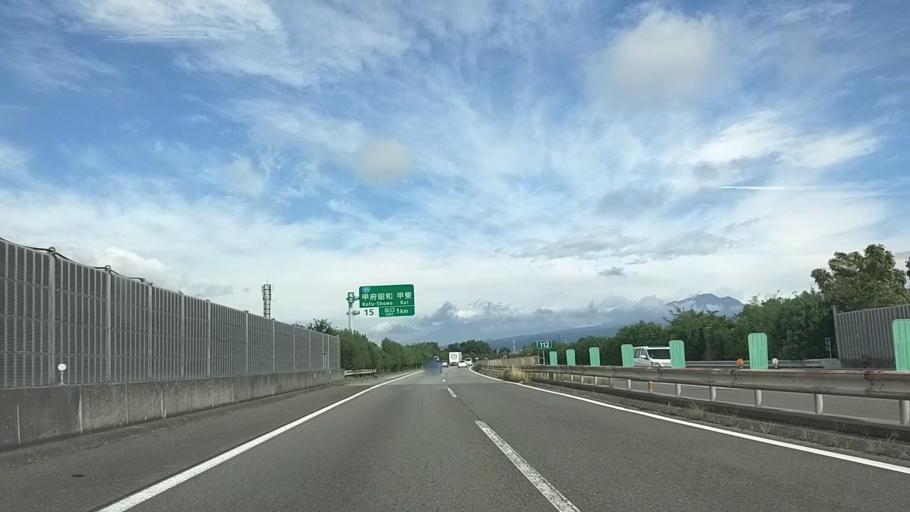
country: JP
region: Yamanashi
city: Kofu-shi
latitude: 35.6328
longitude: 138.5405
